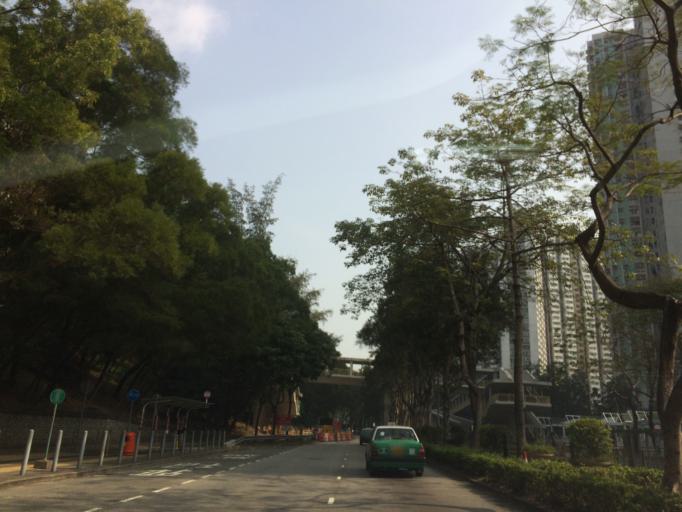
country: HK
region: Tai Po
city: Tai Po
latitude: 22.4559
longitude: 114.1731
